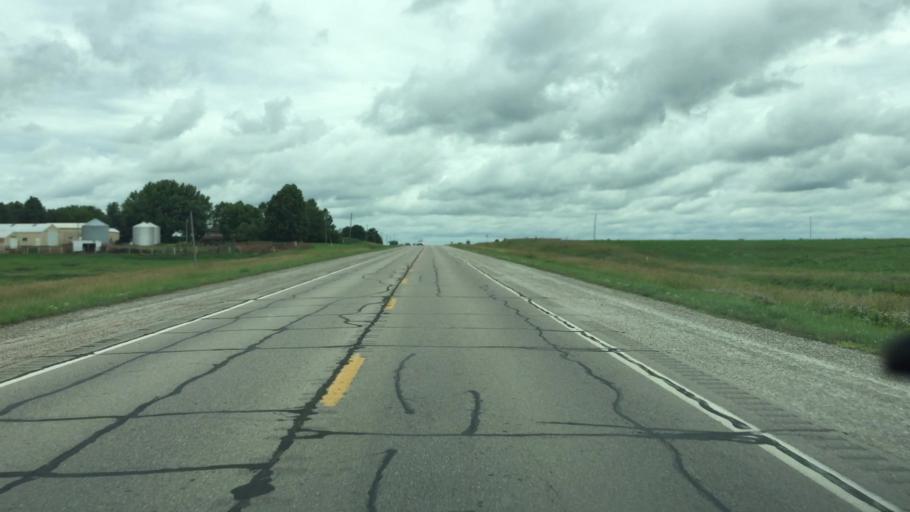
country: US
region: Iowa
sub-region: Jasper County
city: Monroe
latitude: 41.5491
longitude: -93.0970
